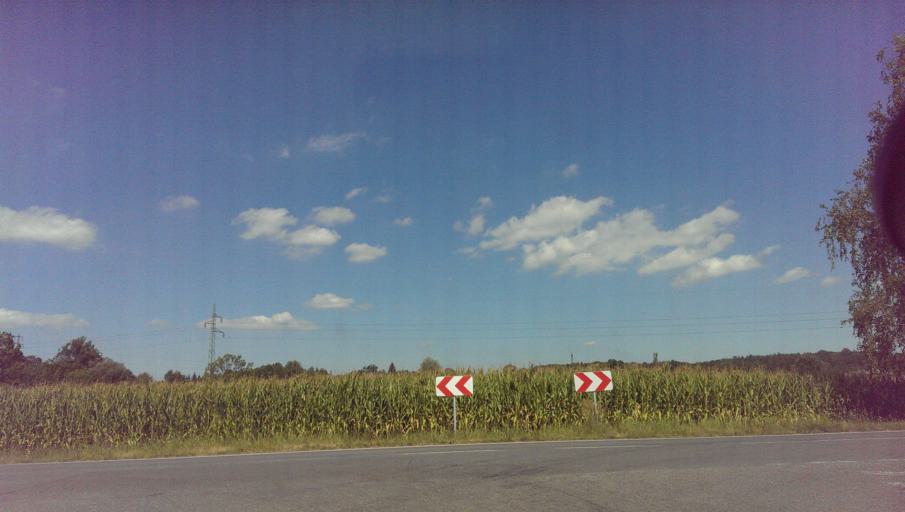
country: CZ
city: Frycovice
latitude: 49.6537
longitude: 18.2195
